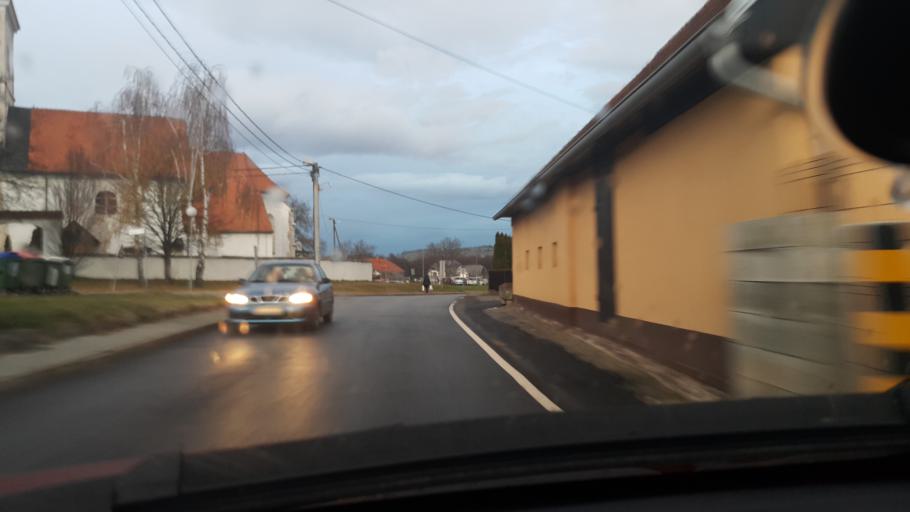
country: SI
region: Miklavz na Dravskem Polju
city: Miklavz na Dravskem Polju
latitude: 46.5351
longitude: 15.6876
